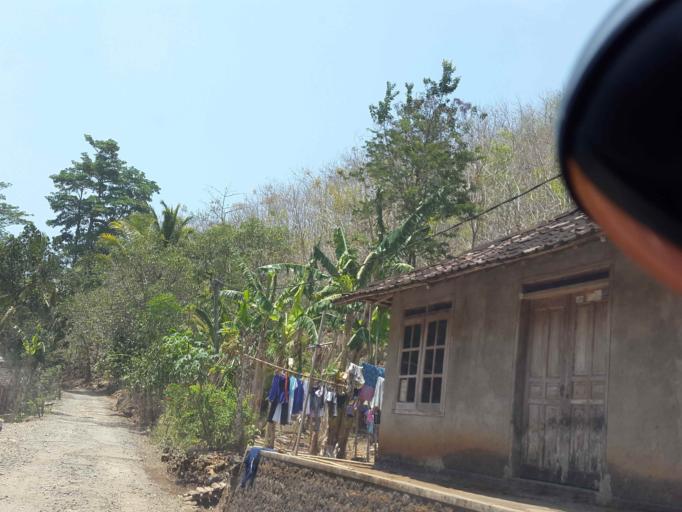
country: ID
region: East Java
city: Krajan
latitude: -8.2005
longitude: 110.9590
